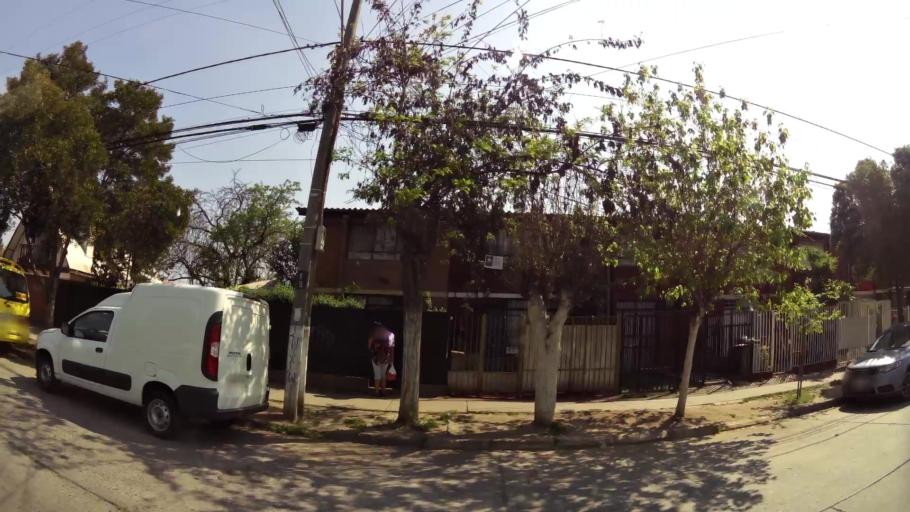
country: CL
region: Santiago Metropolitan
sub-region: Provincia de Santiago
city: La Pintana
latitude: -33.5436
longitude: -70.5983
